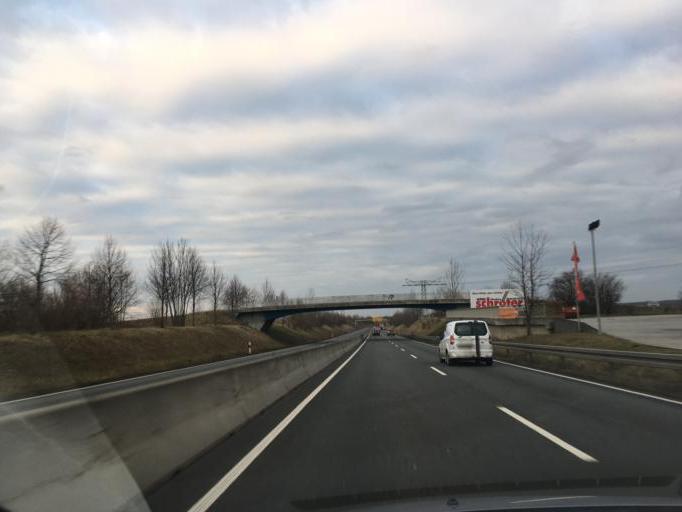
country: DE
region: Thuringia
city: Gerstenberg
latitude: 51.0156
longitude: 12.4542
